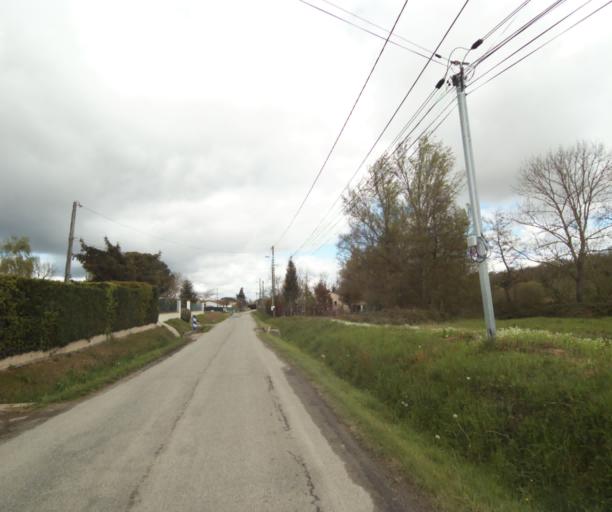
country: FR
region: Midi-Pyrenees
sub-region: Departement de l'Ariege
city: Saverdun
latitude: 43.2206
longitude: 1.5722
